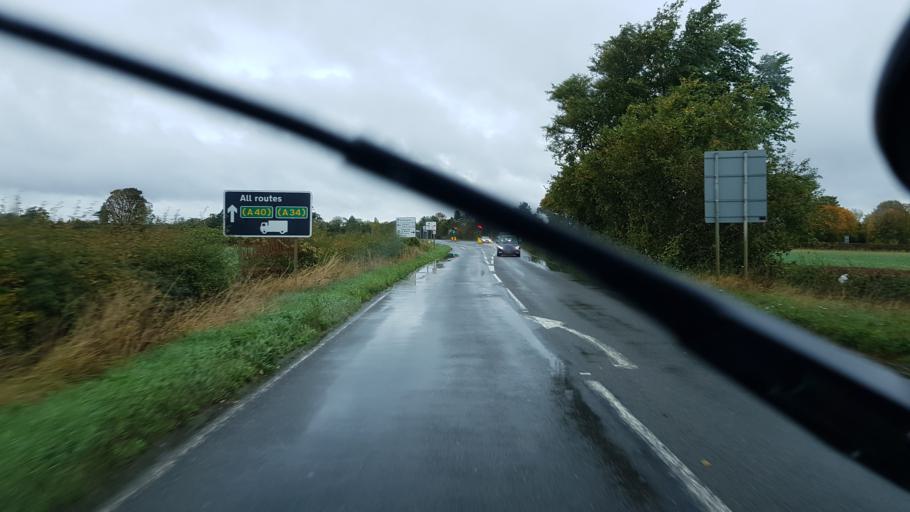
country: GB
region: England
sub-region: Oxfordshire
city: Ducklington
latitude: 51.7484
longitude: -1.4538
